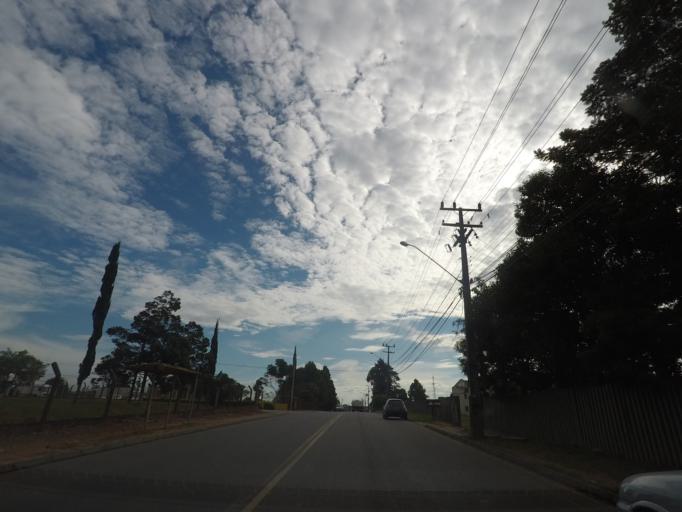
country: BR
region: Parana
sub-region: Araucaria
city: Araucaria
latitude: -25.6413
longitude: -49.3048
